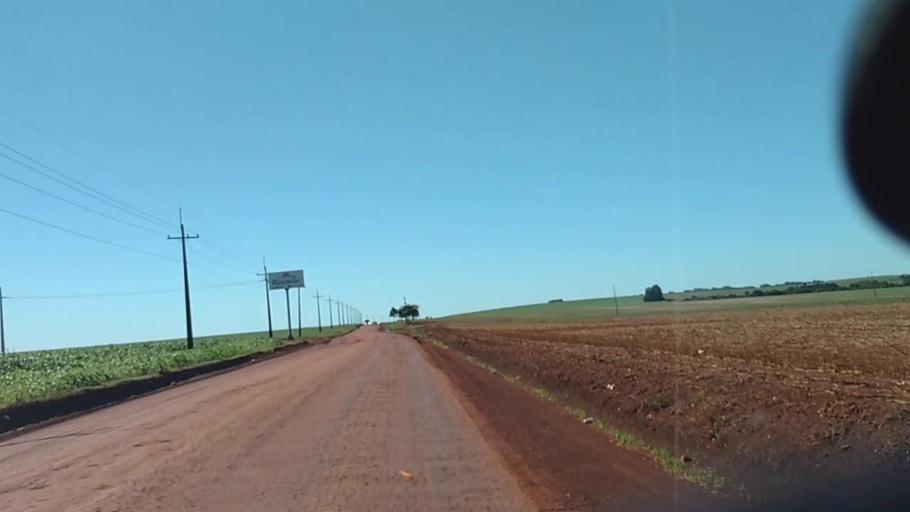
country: PY
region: Alto Parana
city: Naranjal
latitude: -25.9403
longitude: -55.2958
